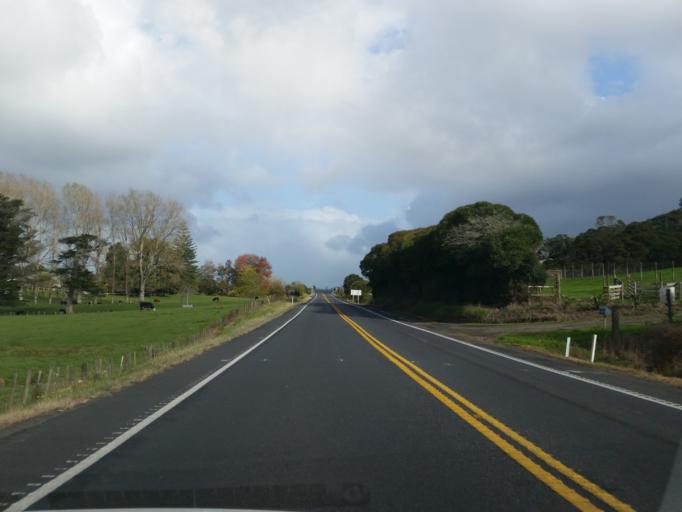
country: NZ
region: Auckland
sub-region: Auckland
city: Pukekohe East
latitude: -37.2124
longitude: 175.0746
